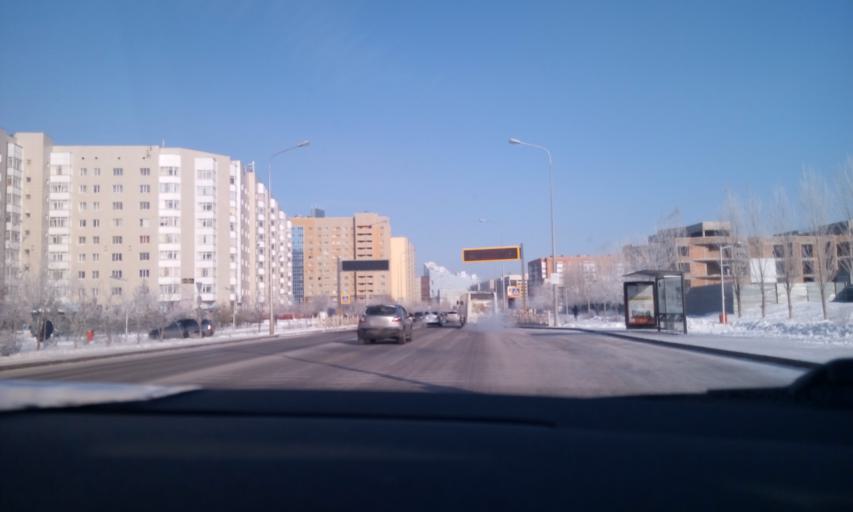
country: KZ
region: Astana Qalasy
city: Astana
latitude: 51.1189
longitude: 71.4196
